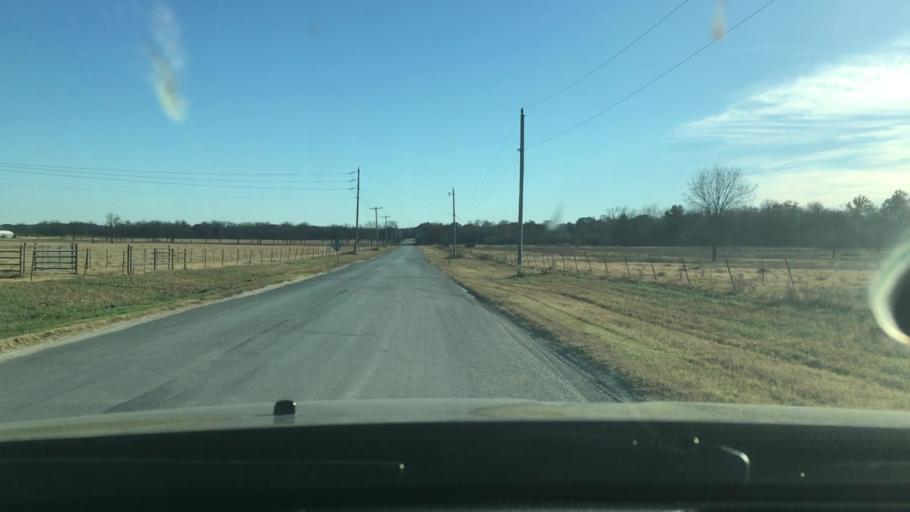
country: US
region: Oklahoma
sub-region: Murray County
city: Davis
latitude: 34.4984
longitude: -97.1585
